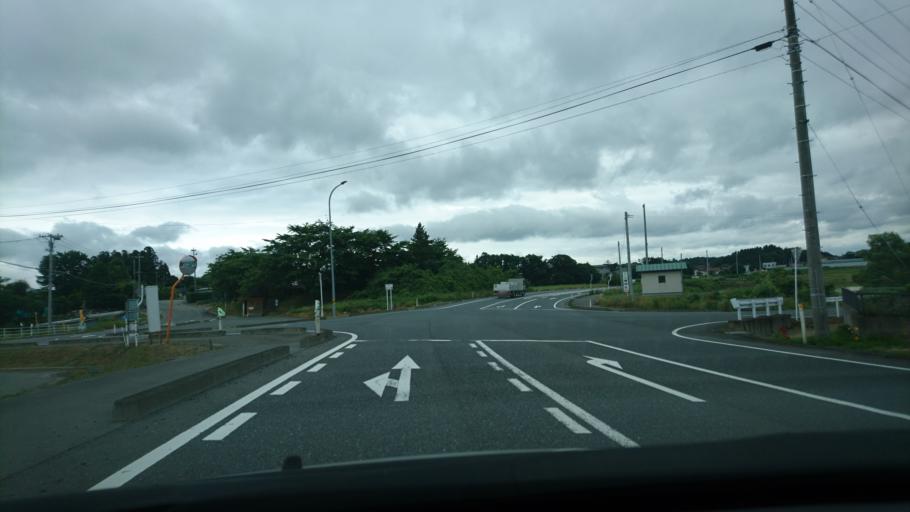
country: JP
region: Iwate
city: Ichinoseki
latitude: 38.7470
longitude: 141.2558
